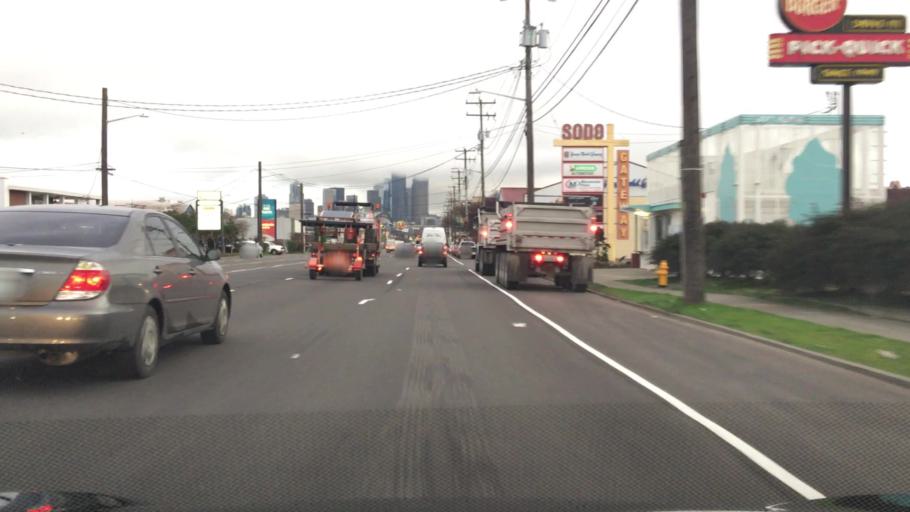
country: US
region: Washington
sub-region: King County
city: Seattle
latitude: 47.5756
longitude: -122.3290
